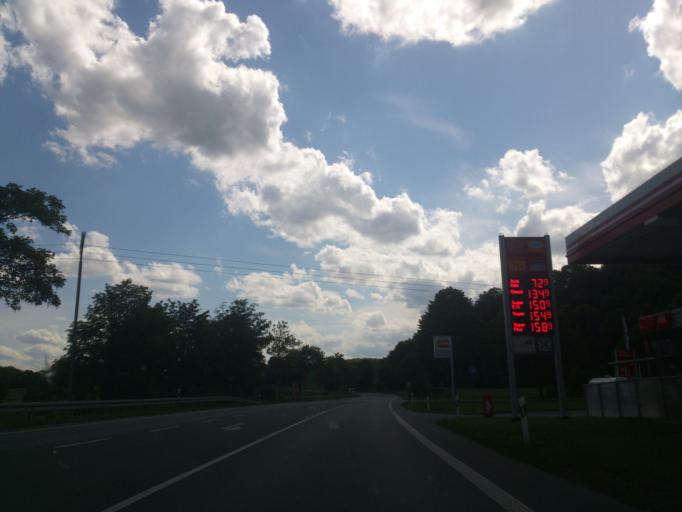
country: DE
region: North Rhine-Westphalia
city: Brakel
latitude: 51.6491
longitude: 9.1433
